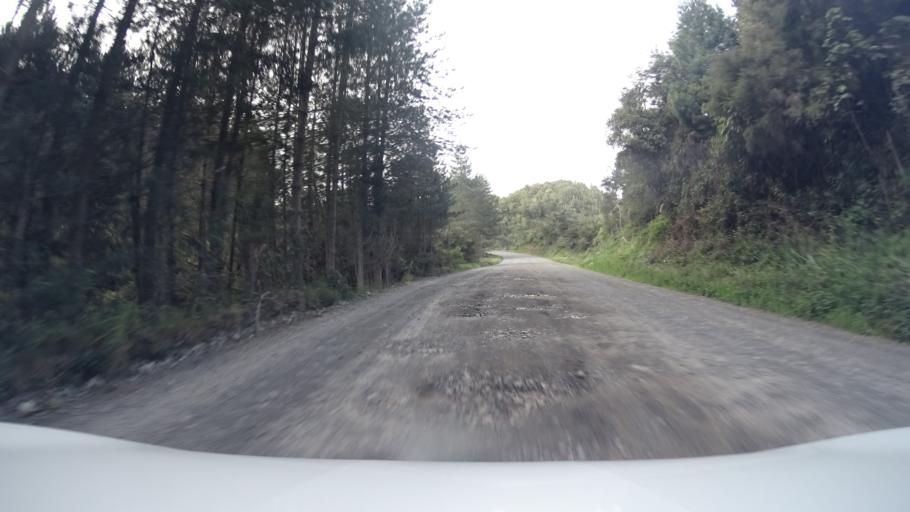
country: NZ
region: Bay of Plenty
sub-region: Rotorua District
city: Rotorua
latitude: -38.3279
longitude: 176.3751
